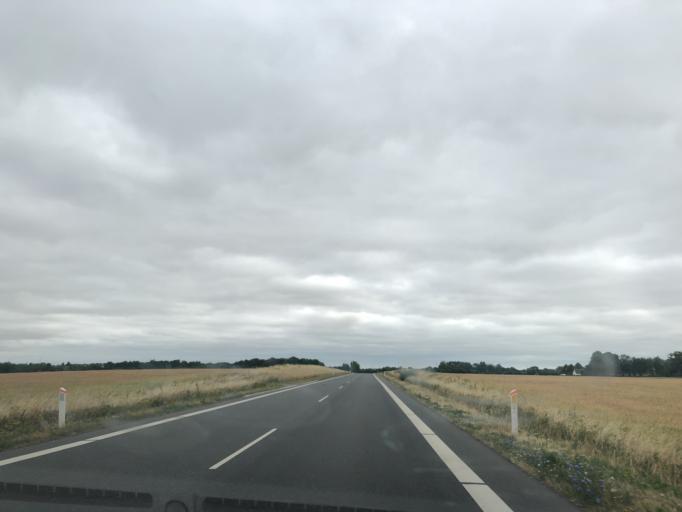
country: DK
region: Zealand
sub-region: Slagelse Kommune
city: Skaelskor
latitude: 55.2447
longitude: 11.3208
